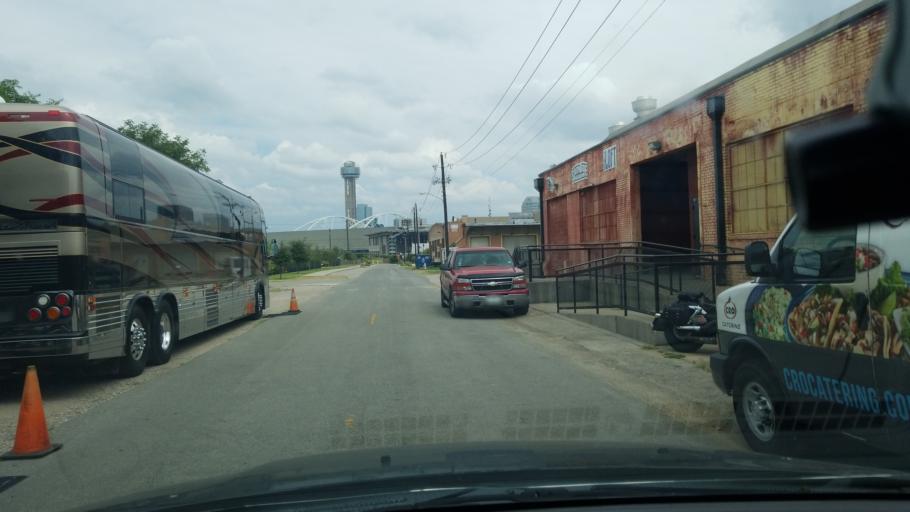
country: US
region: Texas
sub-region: Dallas County
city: Dallas
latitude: 32.7684
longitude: -96.7984
